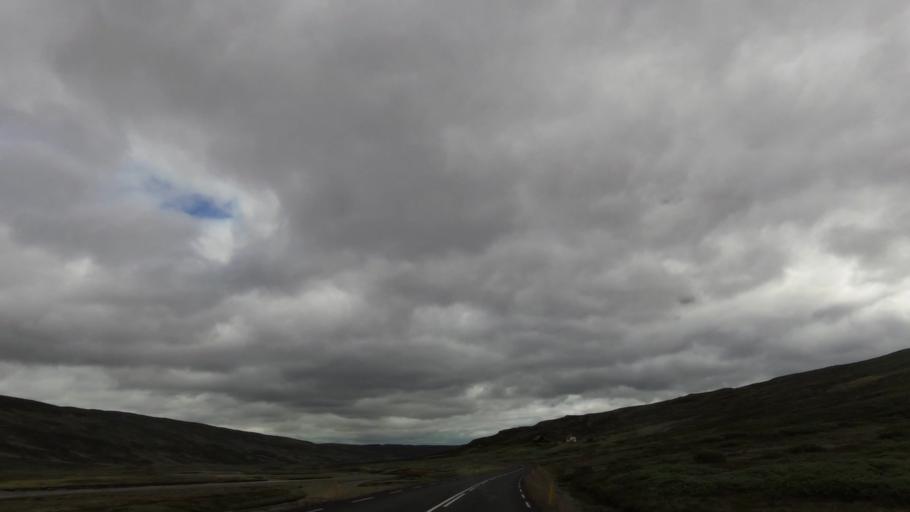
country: IS
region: West
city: Stykkisholmur
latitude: 65.7595
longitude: -21.8526
